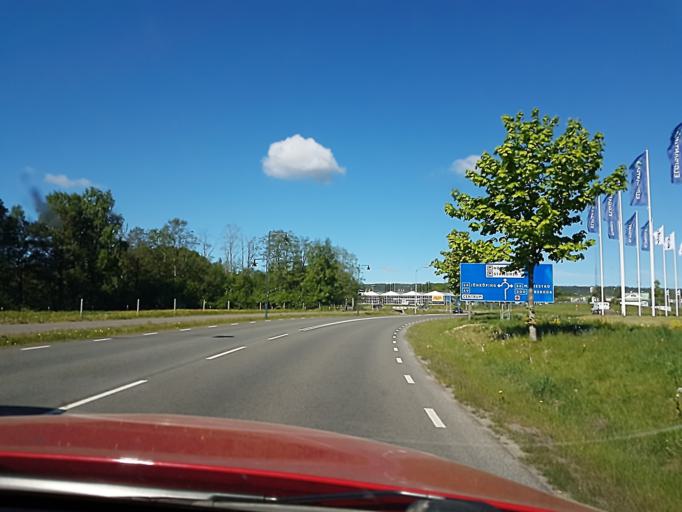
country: SE
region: Vaestra Goetaland
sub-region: Skovde Kommun
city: Skoevde
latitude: 58.4072
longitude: 13.8802
